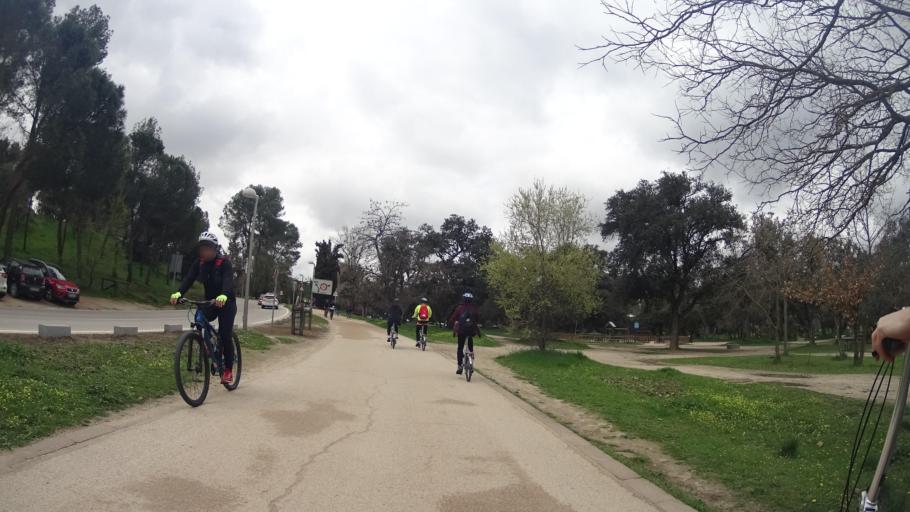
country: ES
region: Madrid
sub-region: Provincia de Madrid
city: Latina
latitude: 40.4109
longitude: -3.7587
